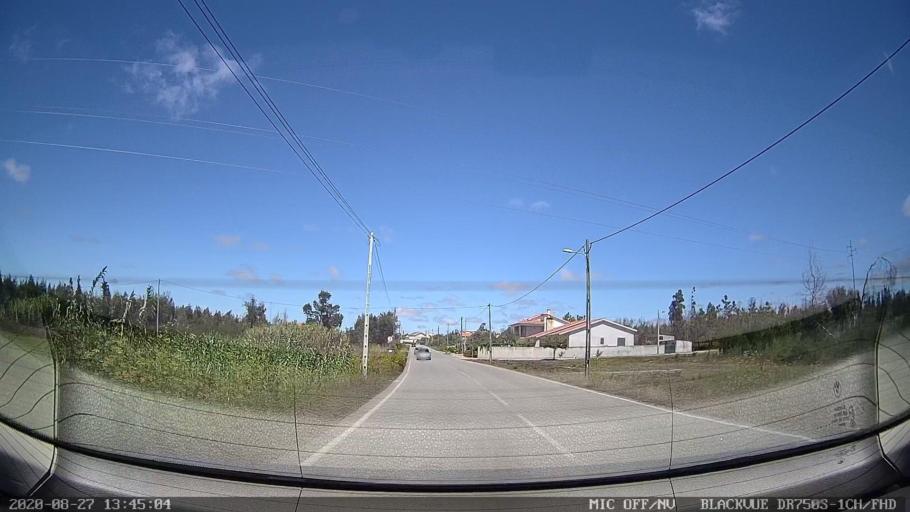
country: PT
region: Coimbra
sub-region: Mira
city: Mira
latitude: 40.4086
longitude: -8.7345
